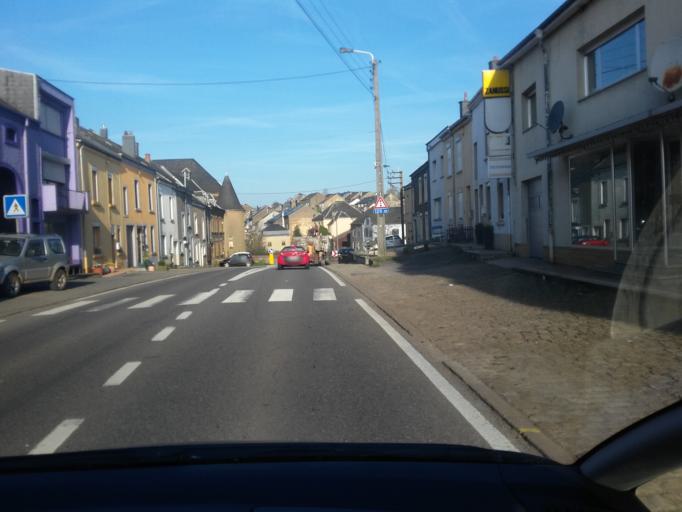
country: BE
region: Wallonia
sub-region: Province du Luxembourg
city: Virton
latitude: 49.5802
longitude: 5.5785
